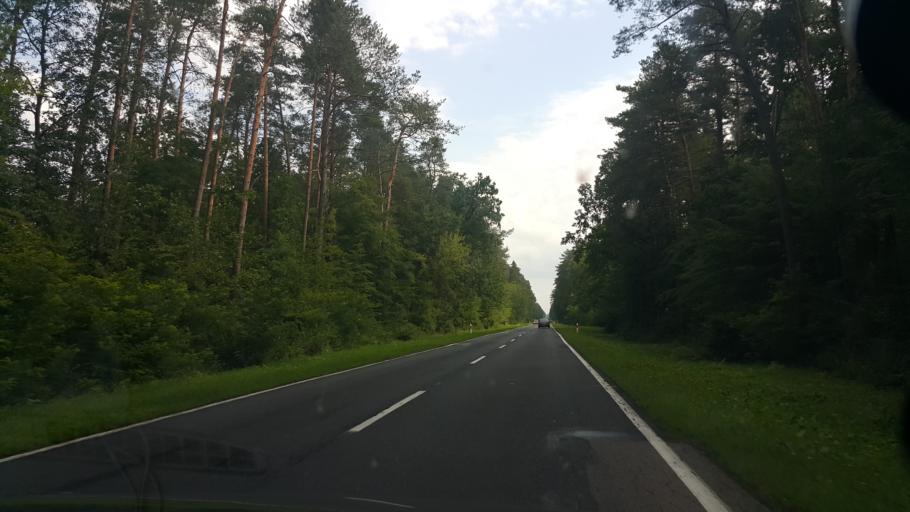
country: PL
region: Lublin Voivodeship
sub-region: Powiat wlodawski
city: Hansk
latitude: 51.5042
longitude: 23.3763
